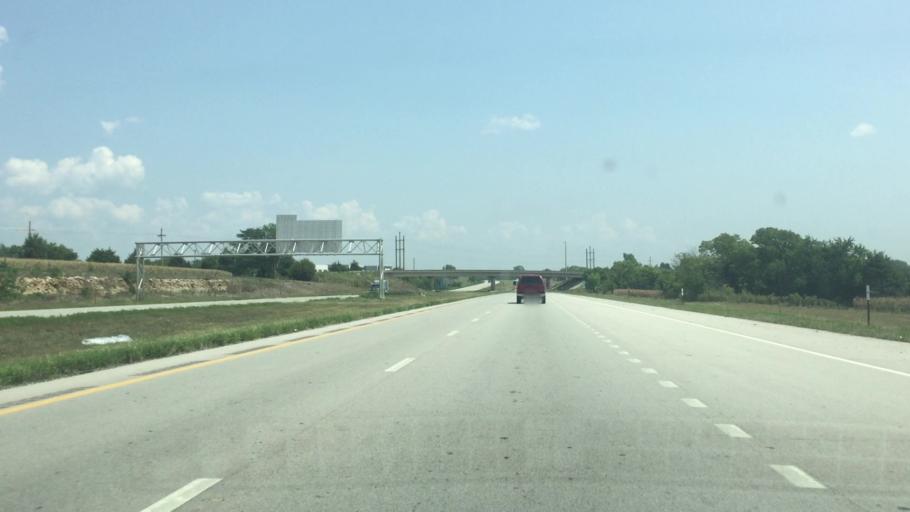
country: US
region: Kansas
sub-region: Johnson County
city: Gardner
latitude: 38.7654
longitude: -94.9524
